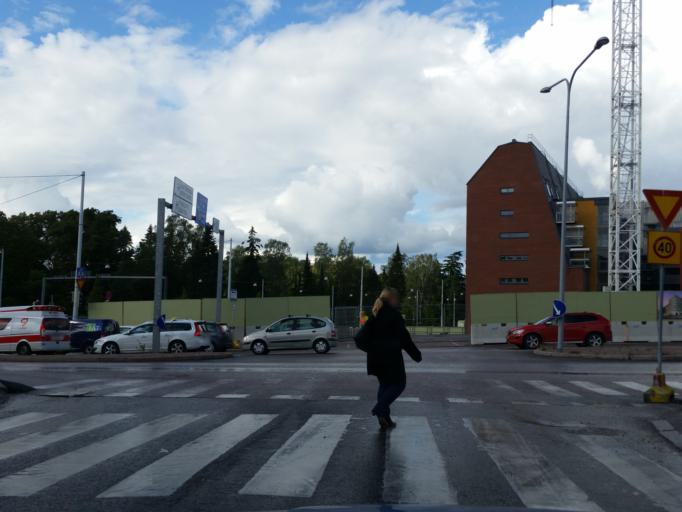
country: FI
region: Uusimaa
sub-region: Helsinki
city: Helsinki
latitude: 60.1677
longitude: 24.9223
